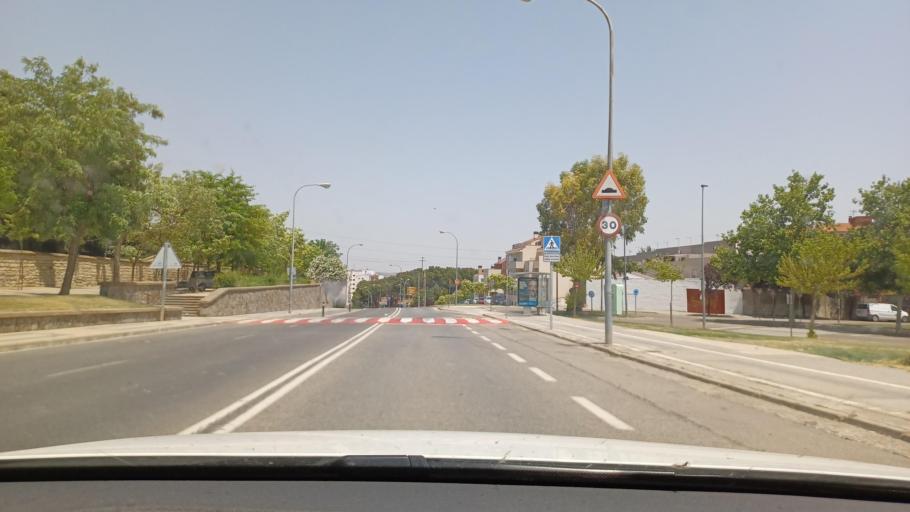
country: ES
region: Navarre
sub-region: Provincia de Navarra
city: Tudela
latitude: 42.0555
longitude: -1.6098
